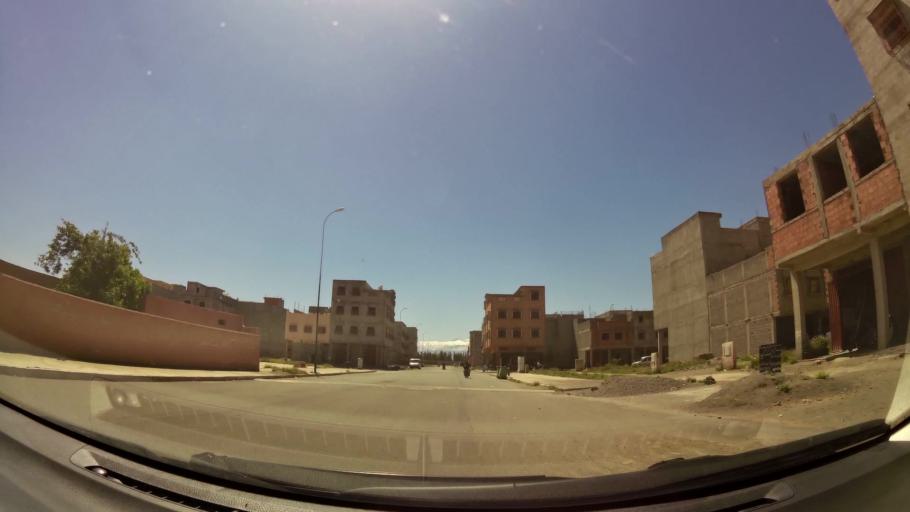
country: MA
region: Marrakech-Tensift-Al Haouz
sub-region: Marrakech
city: Marrakesh
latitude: 31.5519
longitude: -7.9783
